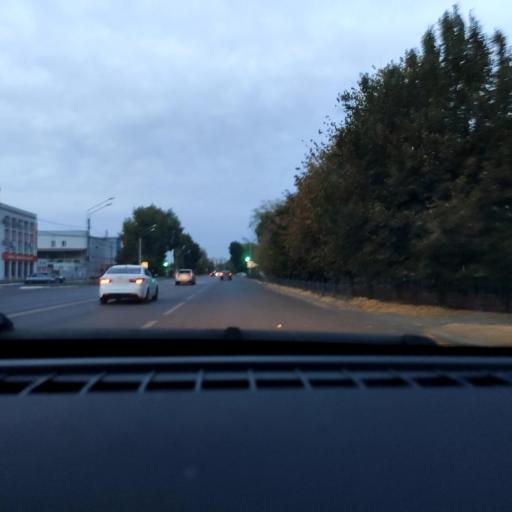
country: RU
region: Voronezj
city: Voronezh
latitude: 51.6510
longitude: 39.2701
